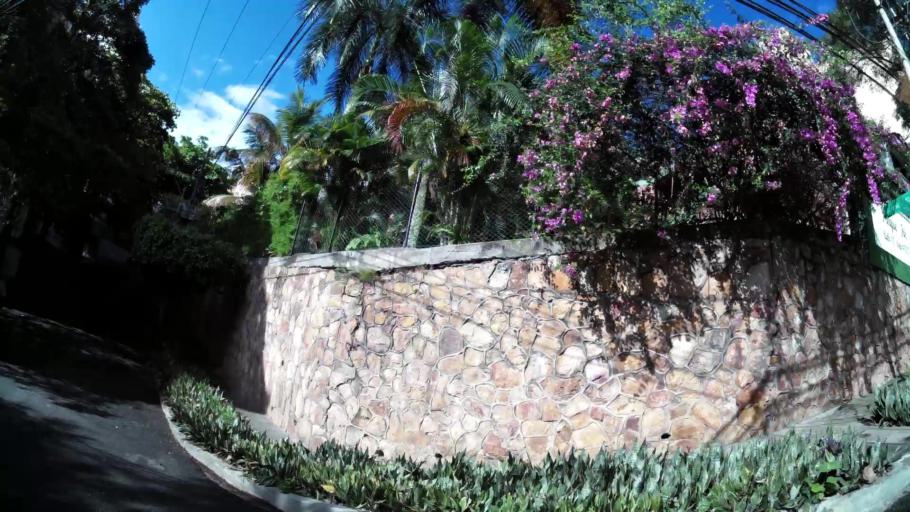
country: CO
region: Valle del Cauca
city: Cali
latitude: 3.4571
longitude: -76.5378
